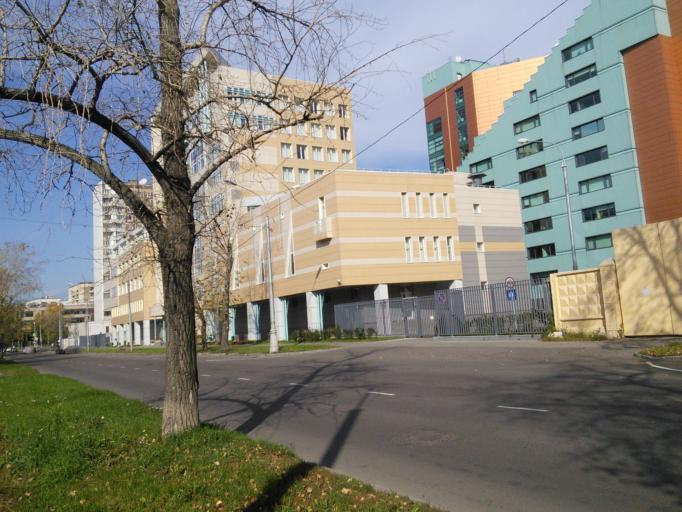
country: RU
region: Moscow
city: Mar'ina Roshcha
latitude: 55.8034
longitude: 37.5812
